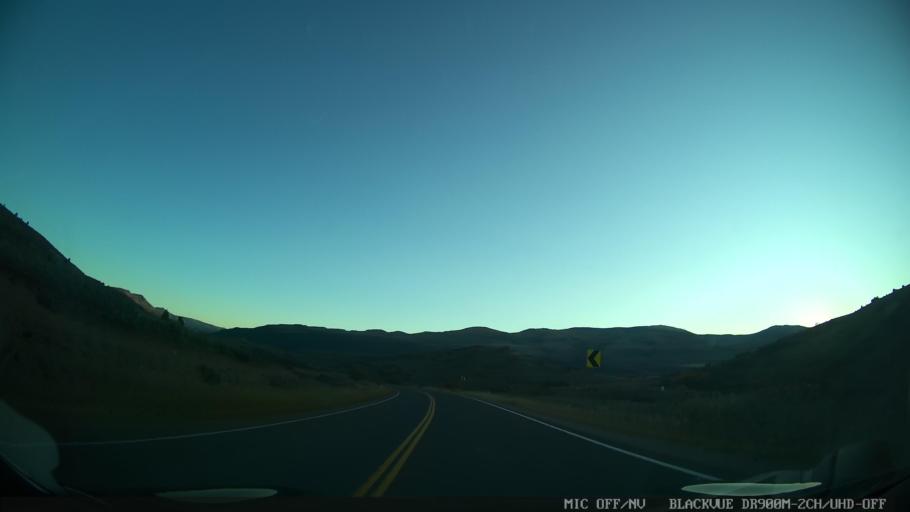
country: US
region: Colorado
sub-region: Eagle County
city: Edwards
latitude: 39.8225
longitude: -106.6438
